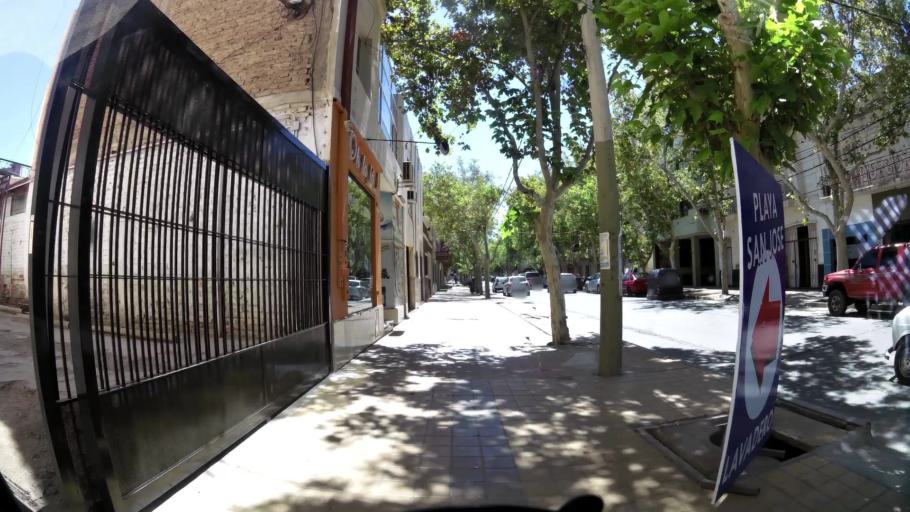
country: AR
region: San Juan
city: San Juan
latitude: -31.5358
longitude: -68.5203
